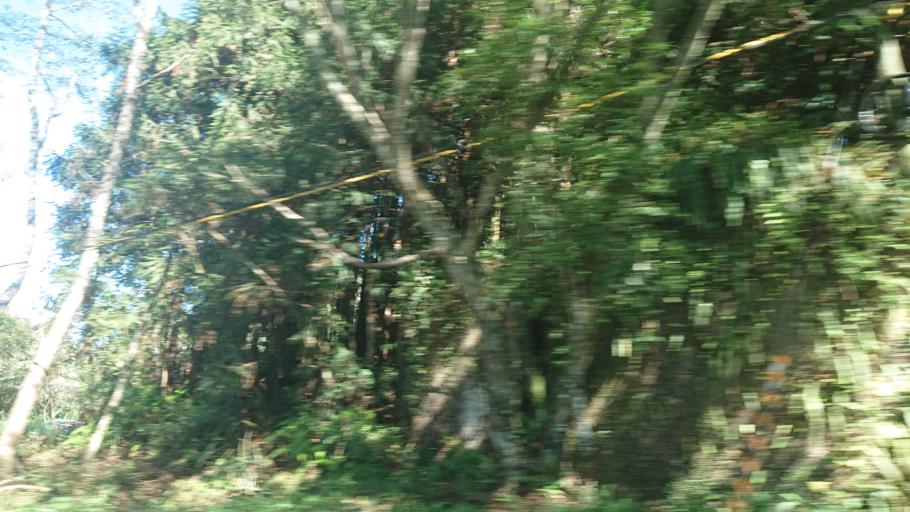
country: TW
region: Taiwan
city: Lugu
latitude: 23.4914
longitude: 120.7916
